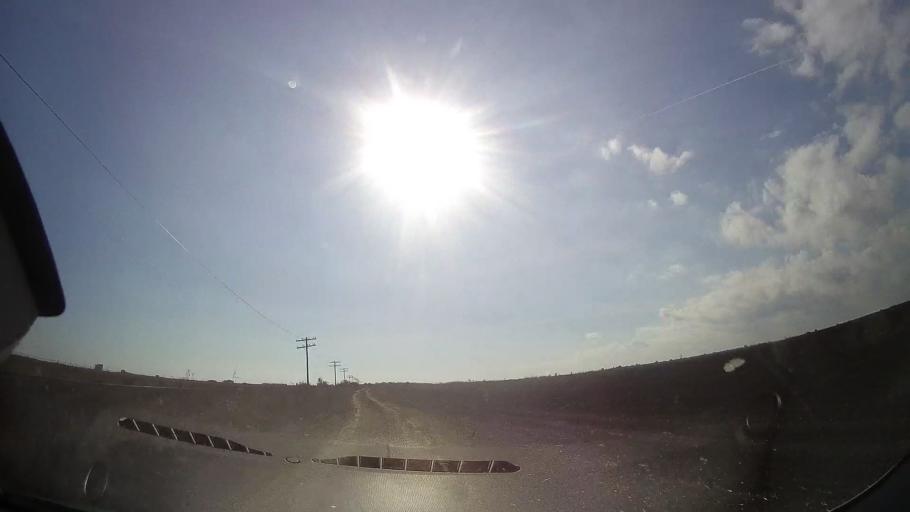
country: RO
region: Constanta
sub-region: Comuna Tuzla
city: Tuzla
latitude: 43.9801
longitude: 28.6444
